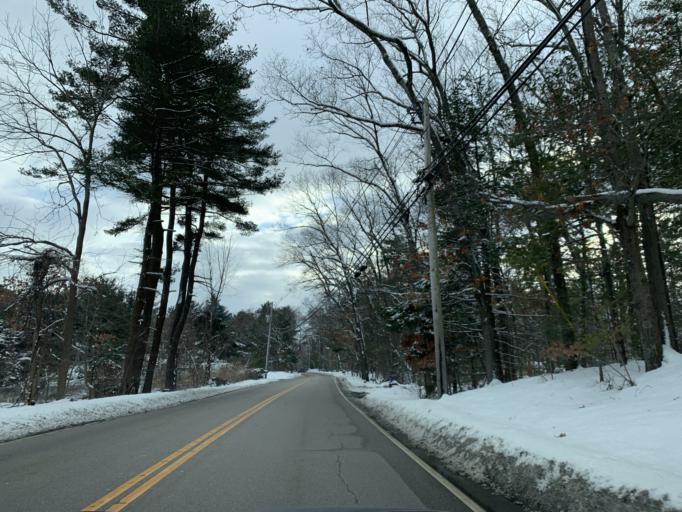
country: US
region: Massachusetts
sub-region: Norfolk County
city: Bellingham
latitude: 42.0483
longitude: -71.4374
